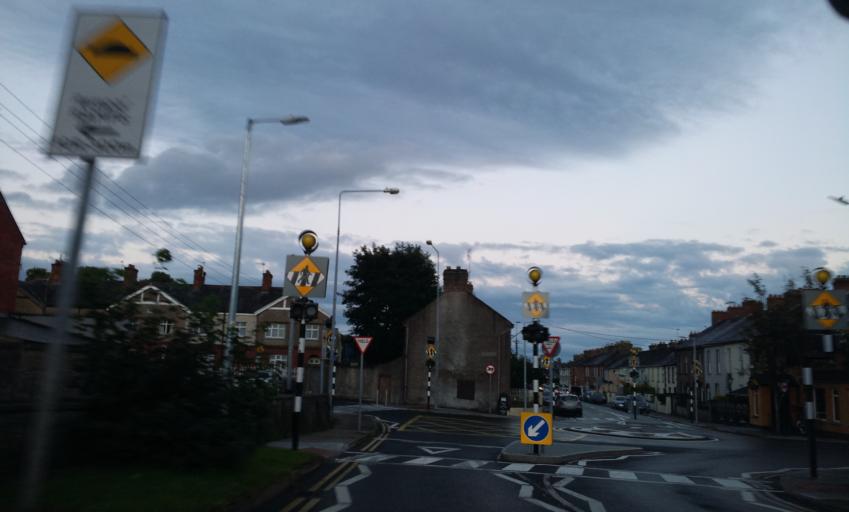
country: IE
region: Munster
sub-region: County Limerick
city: Luimneach
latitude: 52.6515
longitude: -8.6403
